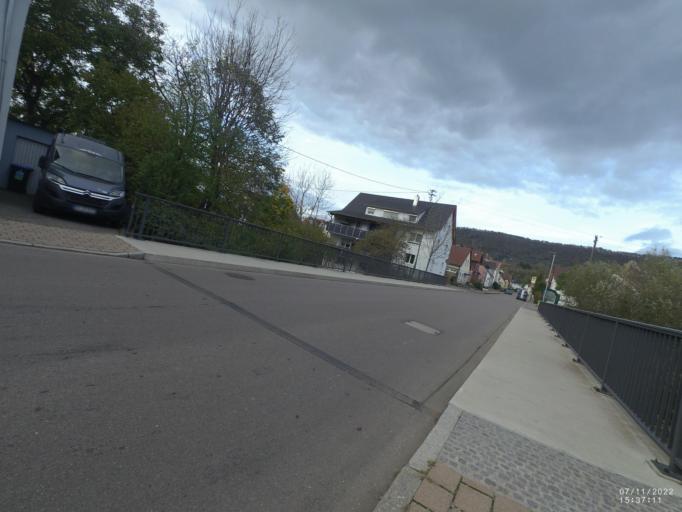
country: DE
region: Baden-Wuerttemberg
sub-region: Regierungsbezirk Stuttgart
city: Kuchen
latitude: 48.6383
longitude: 9.8001
